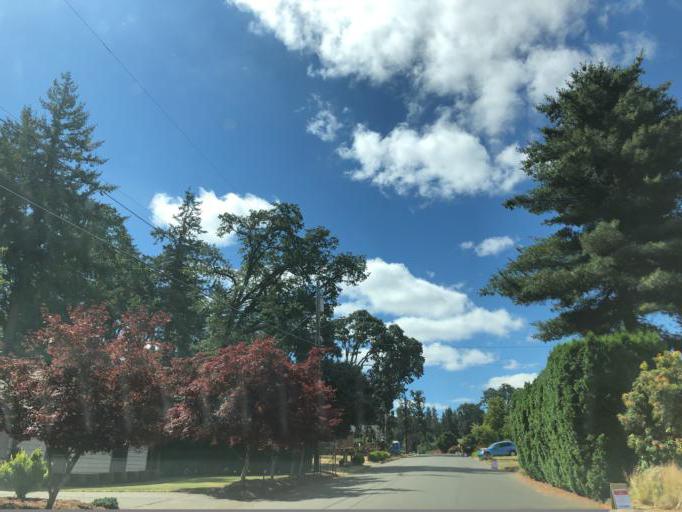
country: US
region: Oregon
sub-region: Marion County
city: Silverton
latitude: 45.0009
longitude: -122.7861
